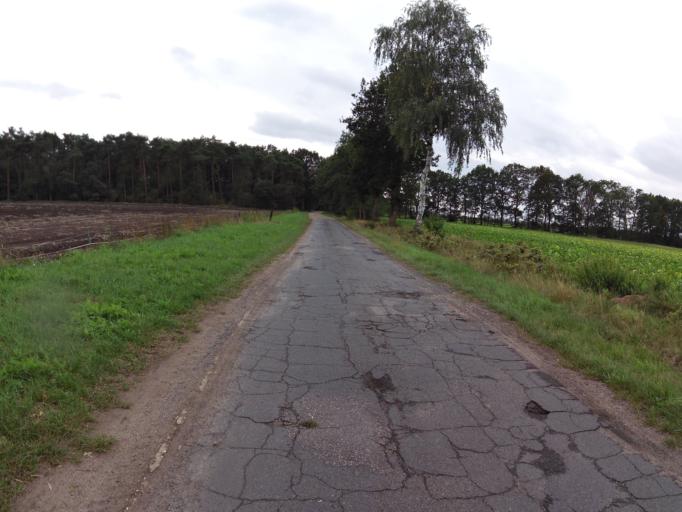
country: DE
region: Lower Saxony
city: Scheessel
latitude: 53.1490
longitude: 9.4494
